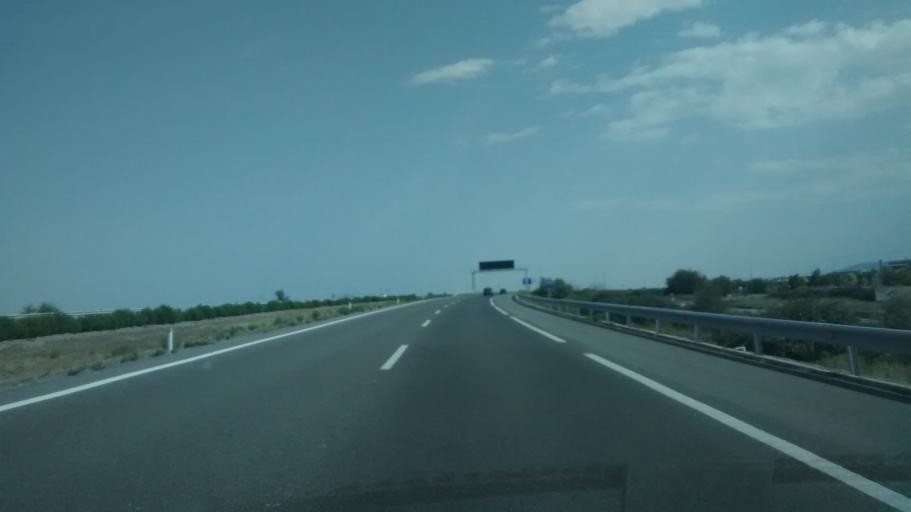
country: ES
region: Navarre
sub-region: Provincia de Navarra
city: Murchante
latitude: 42.0390
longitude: -1.6482
